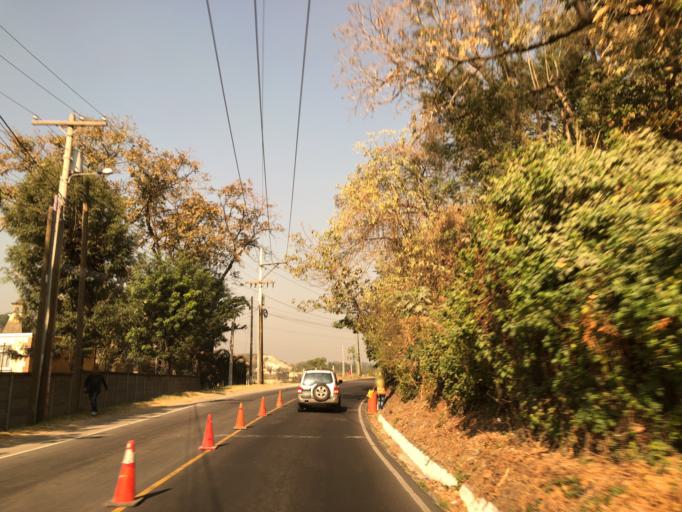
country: GT
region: Guatemala
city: Petapa
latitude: 14.4947
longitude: -90.5398
